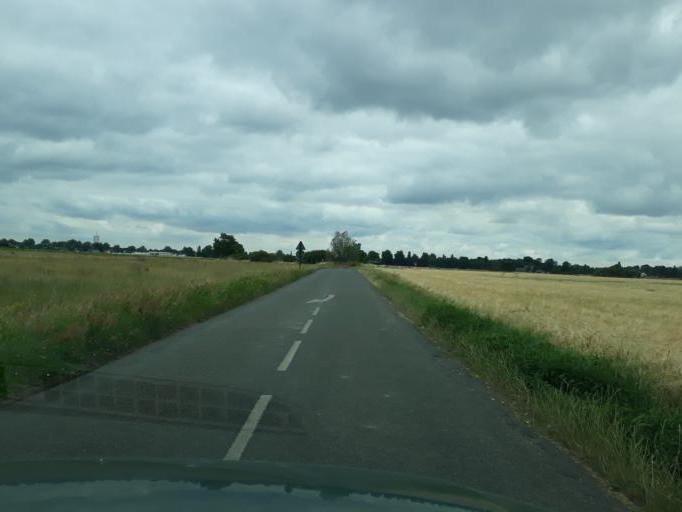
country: FR
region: Centre
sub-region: Departement du Loiret
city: Saint-Denis-en-Val
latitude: 47.8607
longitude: 1.9493
